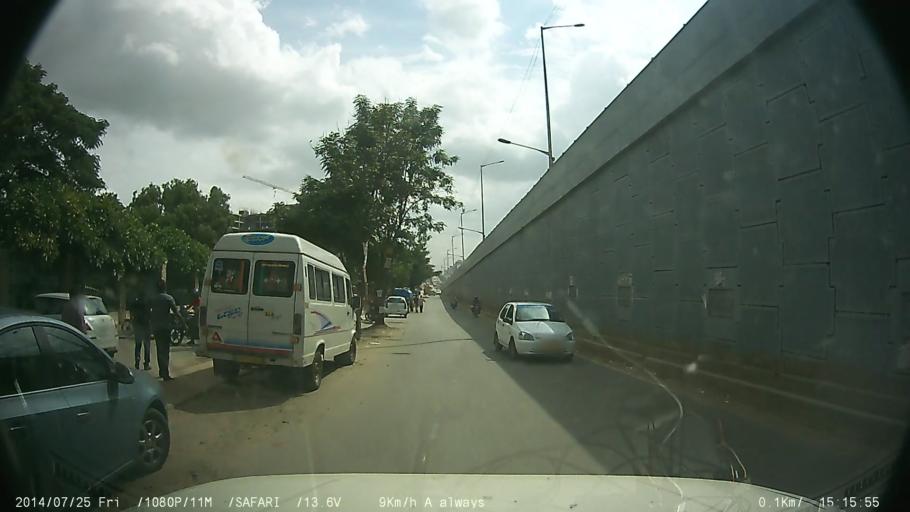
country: IN
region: Karnataka
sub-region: Bangalore Urban
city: Bangalore
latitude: 12.9293
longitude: 77.6843
